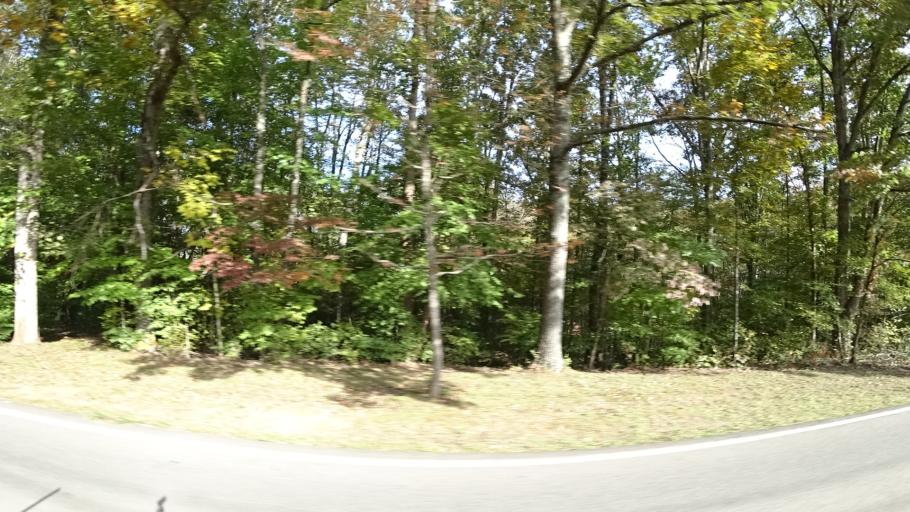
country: US
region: Tennessee
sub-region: Knox County
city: Farragut
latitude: 35.9117
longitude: -84.1864
